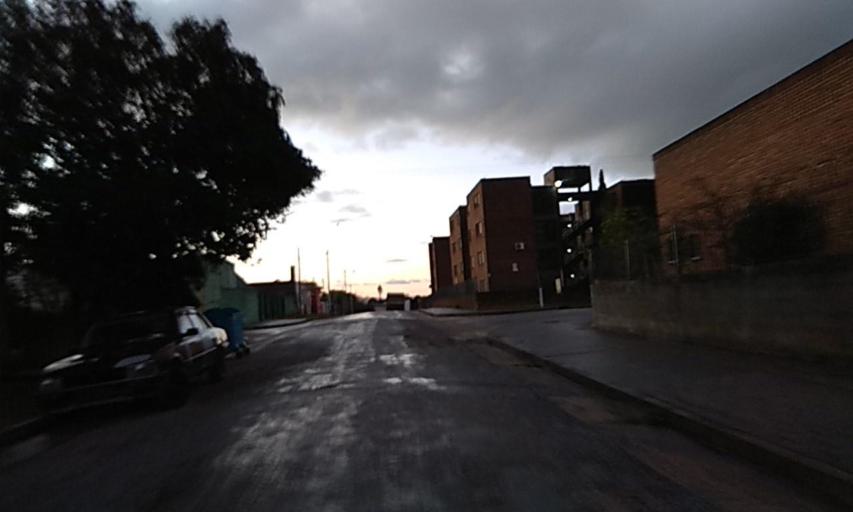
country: UY
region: Florida
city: Florida
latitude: -34.1086
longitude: -56.2099
